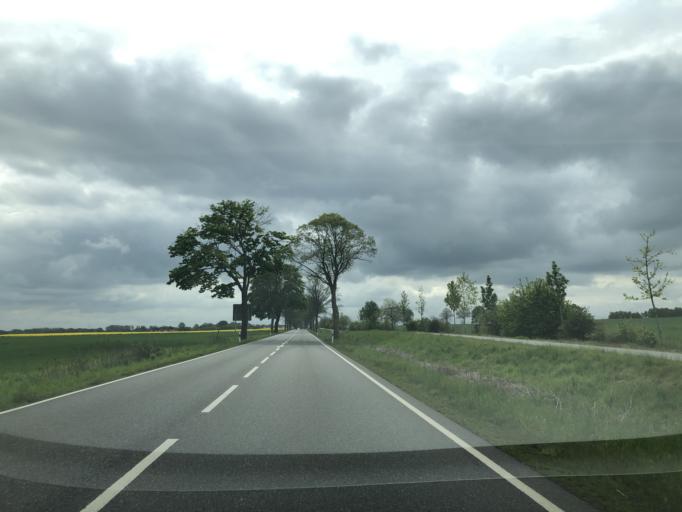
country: DE
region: Mecklenburg-Vorpommern
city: Plau am See
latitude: 53.4632
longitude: 12.2094
